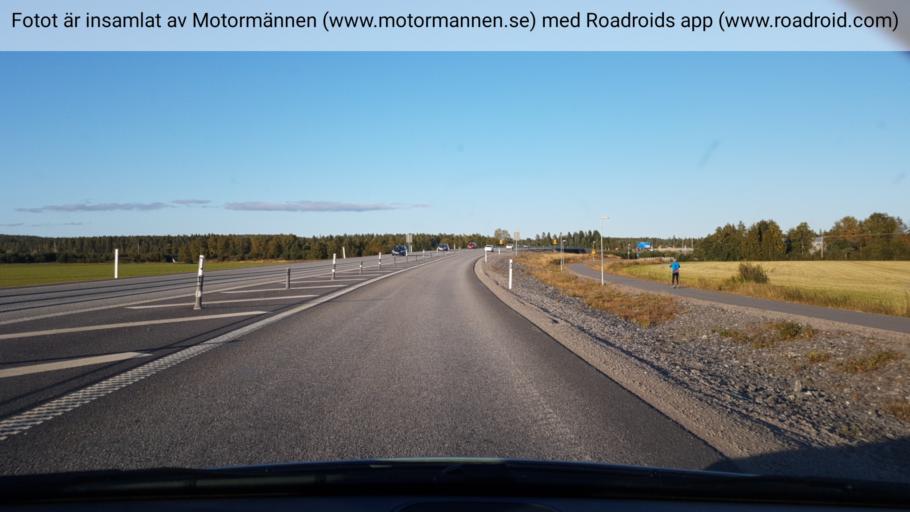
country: SE
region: Vaesterbotten
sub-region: Umea Kommun
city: Roback
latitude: 63.8543
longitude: 20.1943
